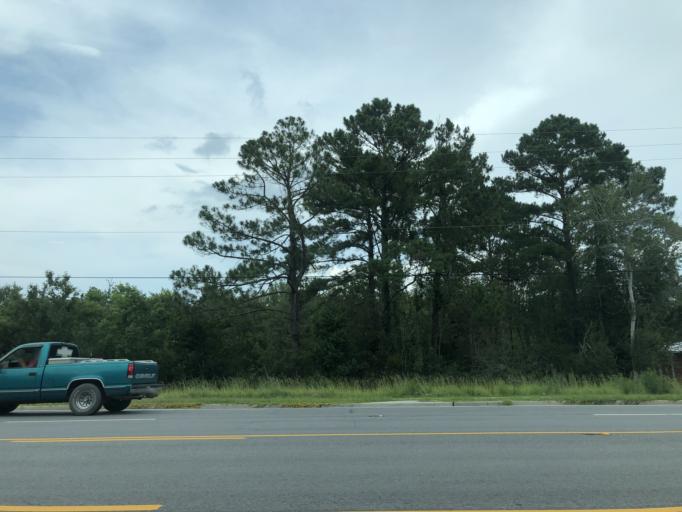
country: US
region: Georgia
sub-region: Wayne County
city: Jesup
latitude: 31.6164
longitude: -81.8925
